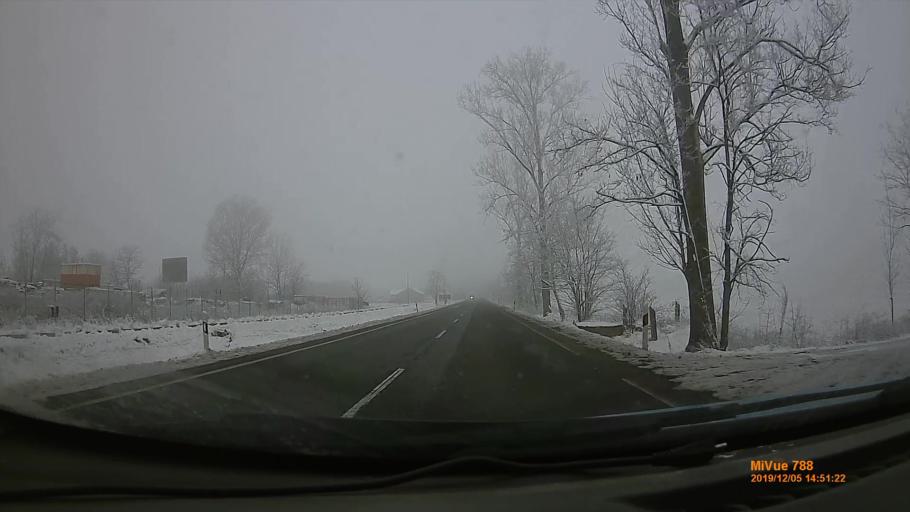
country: HU
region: Szabolcs-Szatmar-Bereg
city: Nyirtelek
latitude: 47.9928
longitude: 21.6587
